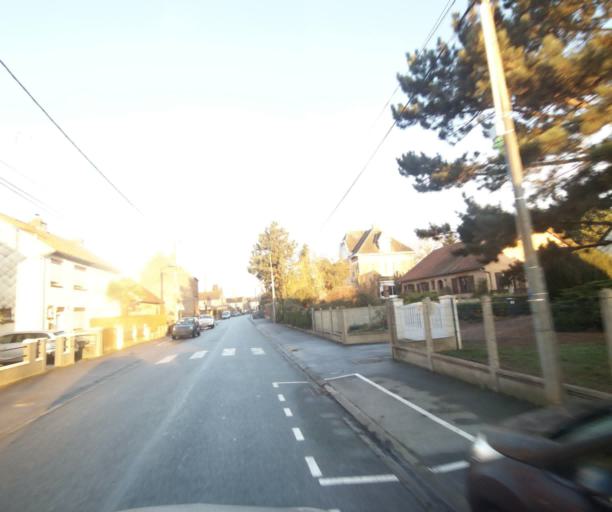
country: FR
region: Nord-Pas-de-Calais
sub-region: Departement du Nord
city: Onnaing
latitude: 50.3832
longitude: 3.6040
